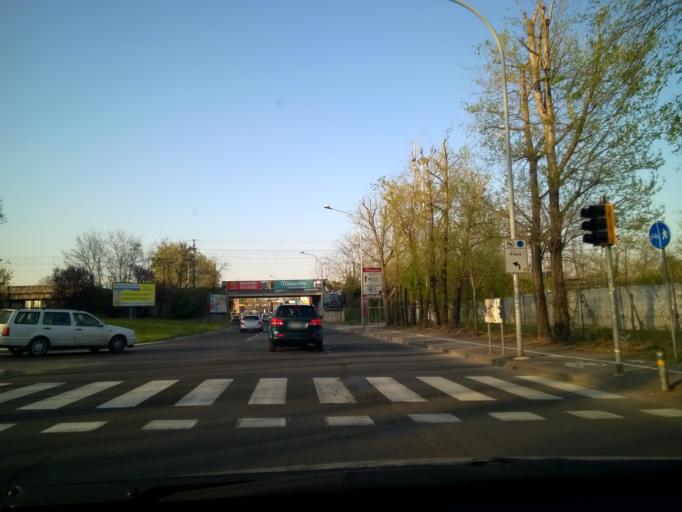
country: IT
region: Emilia-Romagna
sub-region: Provincia di Bologna
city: Bologna
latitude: 44.5177
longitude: 11.3608
